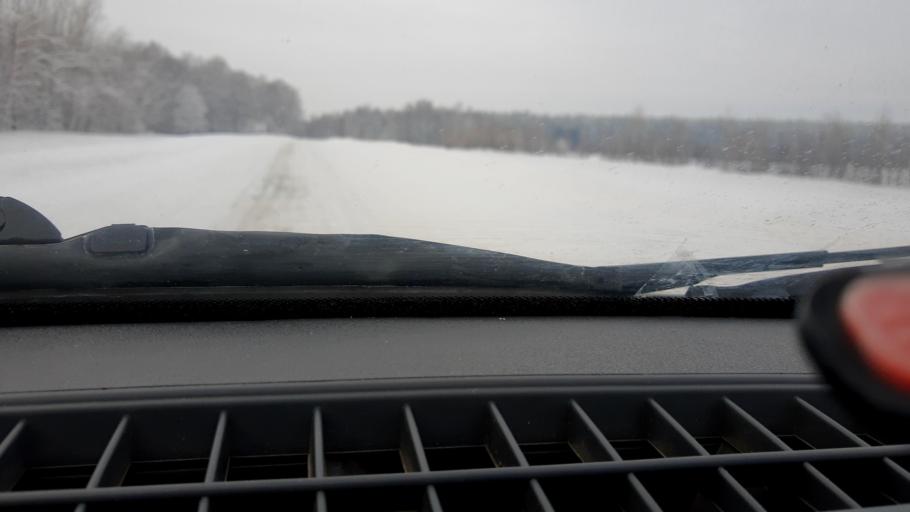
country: RU
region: Bashkortostan
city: Davlekanovo
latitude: 54.5642
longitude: 54.9793
